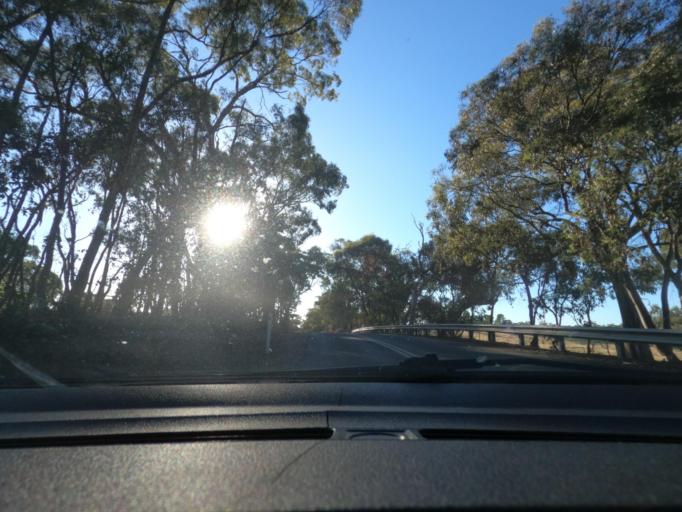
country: AU
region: South Australia
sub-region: Clare and Gilbert Valleys
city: Clare
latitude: -33.9050
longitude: 138.6578
